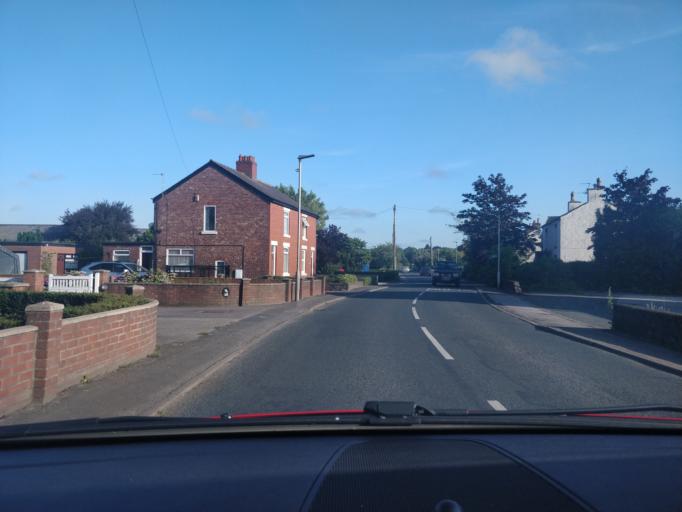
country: GB
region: England
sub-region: Lancashire
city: Banks
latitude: 53.6621
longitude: -2.8797
